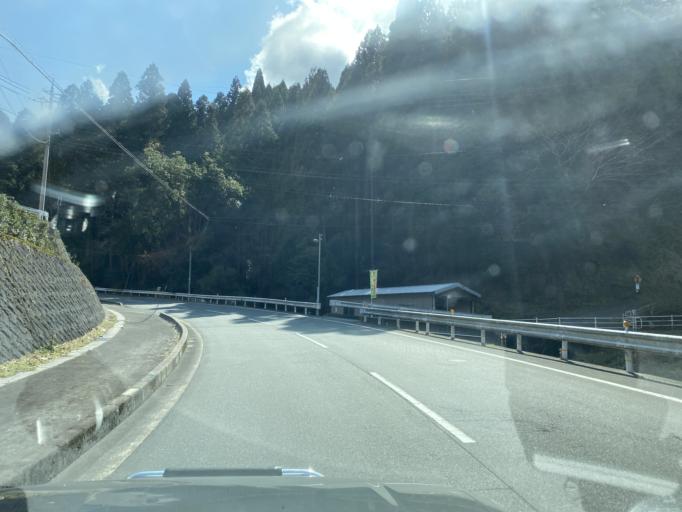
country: JP
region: Nara
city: Nara-shi
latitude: 34.6961
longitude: 135.9509
